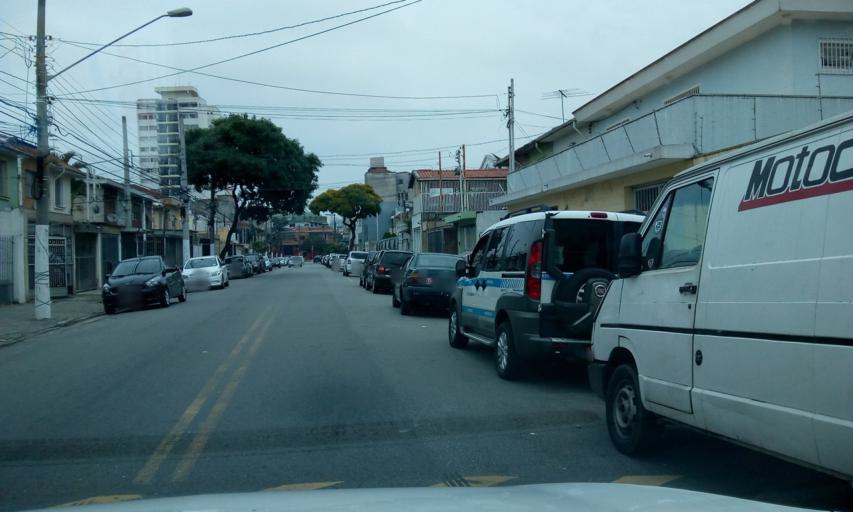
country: BR
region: Sao Paulo
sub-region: Sao Paulo
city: Sao Paulo
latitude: -23.5249
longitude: -46.6053
